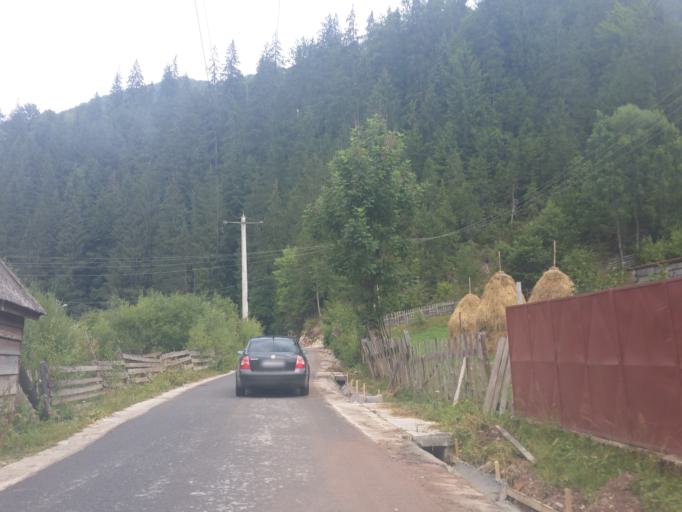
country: RO
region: Alba
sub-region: Comuna Garda de Sus
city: Garda de Sus
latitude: 46.4696
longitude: 22.8194
